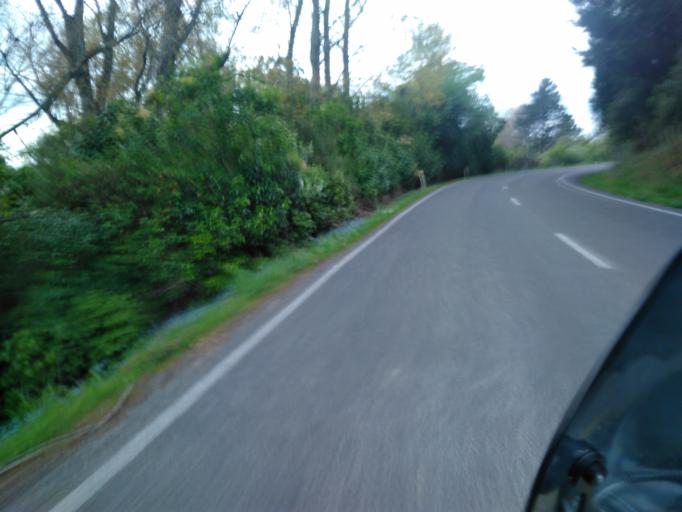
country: NZ
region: Gisborne
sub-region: Gisborne District
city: Gisborne
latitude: -38.6757
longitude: 177.8080
